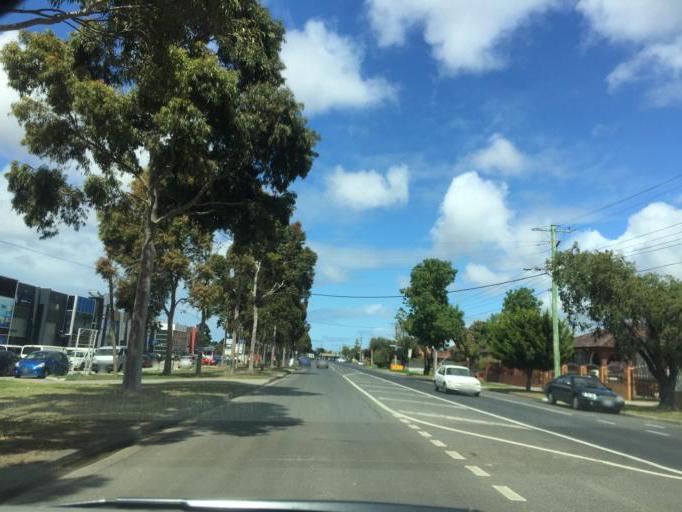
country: AU
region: Victoria
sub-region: Maribyrnong
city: Braybrook
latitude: -37.7745
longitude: 144.8480
